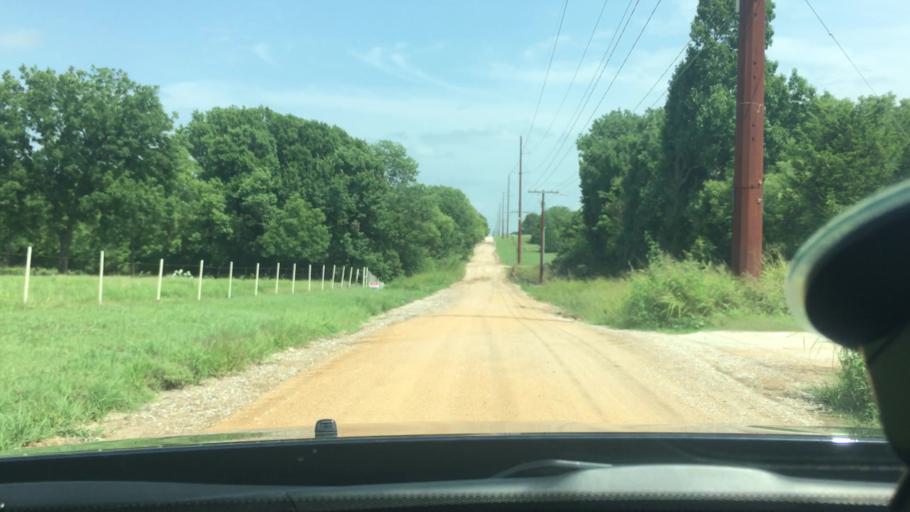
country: US
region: Oklahoma
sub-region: Pontotoc County
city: Ada
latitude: 34.8255
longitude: -96.7409
